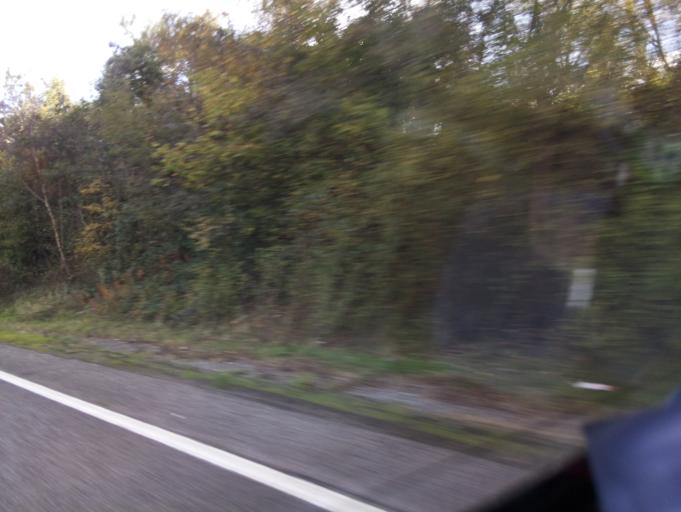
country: GB
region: Wales
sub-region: Merthyr Tydfil County Borough
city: Abercanaid
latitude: 51.7275
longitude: -3.3761
